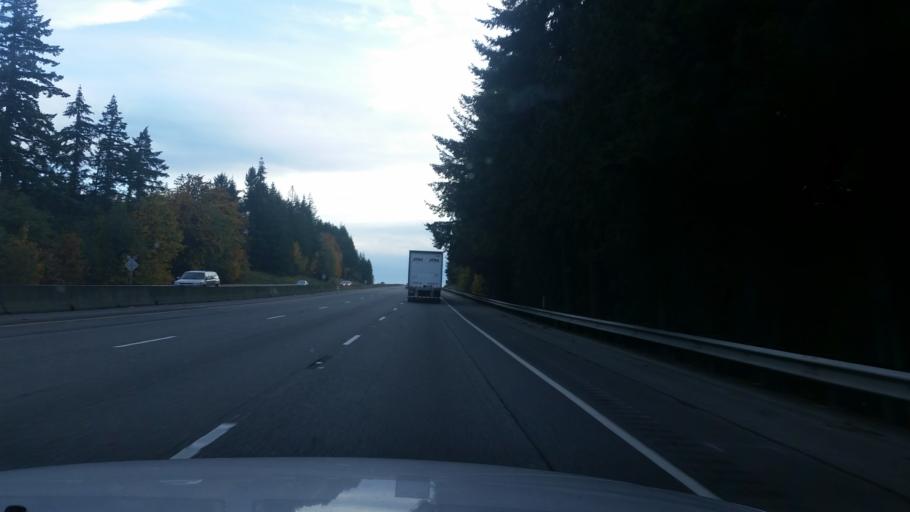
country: US
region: Washington
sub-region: Thurston County
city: Tumwater
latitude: 46.9061
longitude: -122.9561
